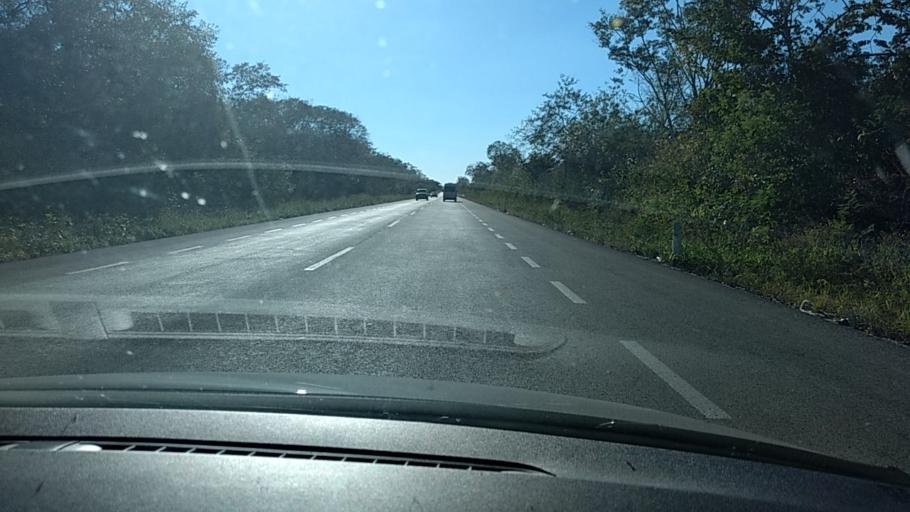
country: MX
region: Yucatan
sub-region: Uayma
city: Uayma
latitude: 20.6281
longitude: -88.3773
